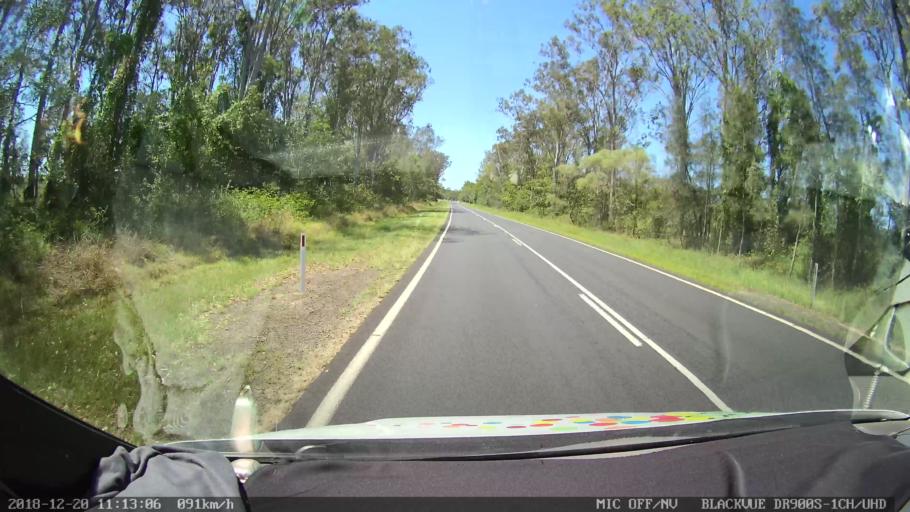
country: AU
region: New South Wales
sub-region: Richmond Valley
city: Casino
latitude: -28.9832
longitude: 153.0094
